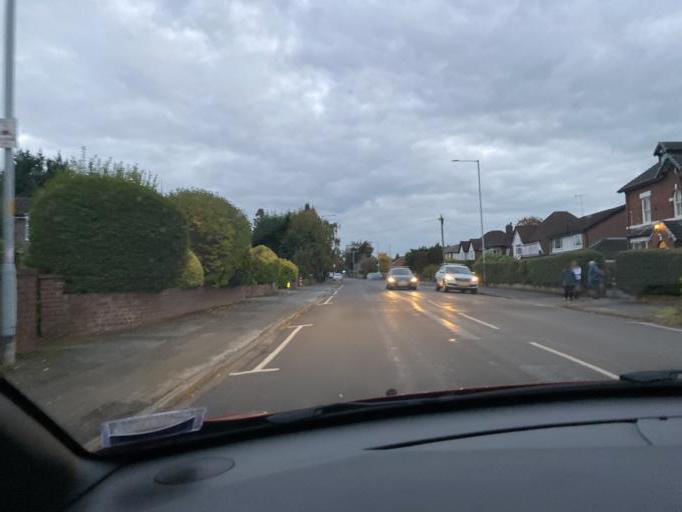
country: GB
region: England
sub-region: Borough of Stockport
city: Hazel Grove
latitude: 53.3704
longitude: -2.1242
